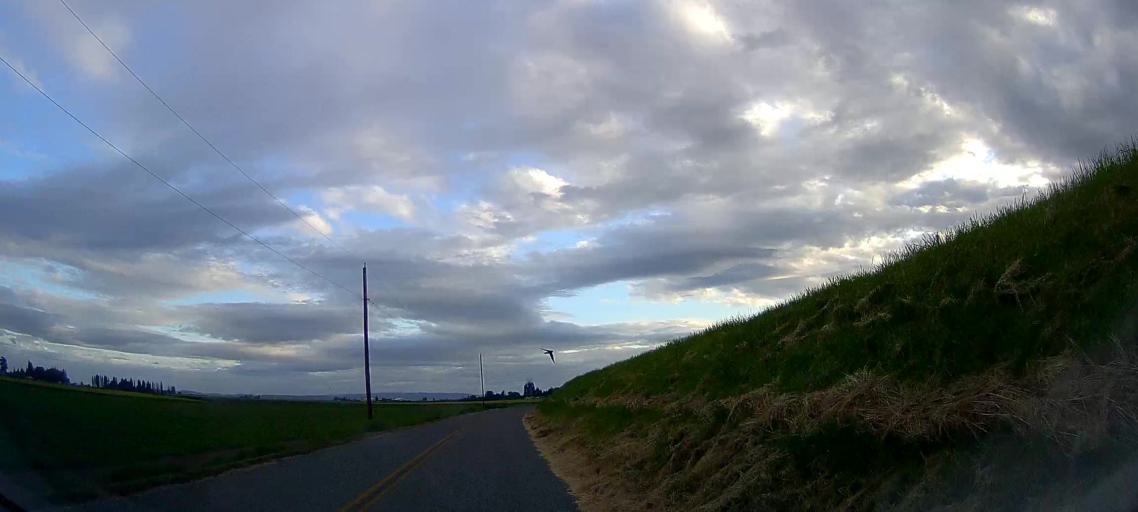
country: US
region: Washington
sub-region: Skagit County
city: Mount Vernon
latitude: 48.3695
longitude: -122.3942
